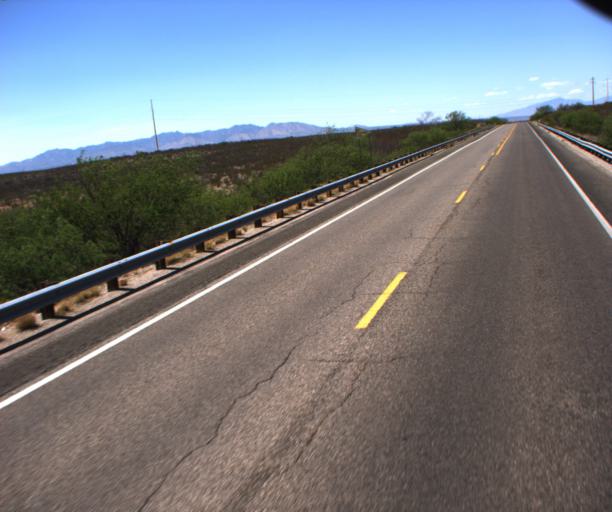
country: US
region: Arizona
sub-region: Cochise County
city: Tombstone
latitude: 31.7715
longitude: -110.1257
